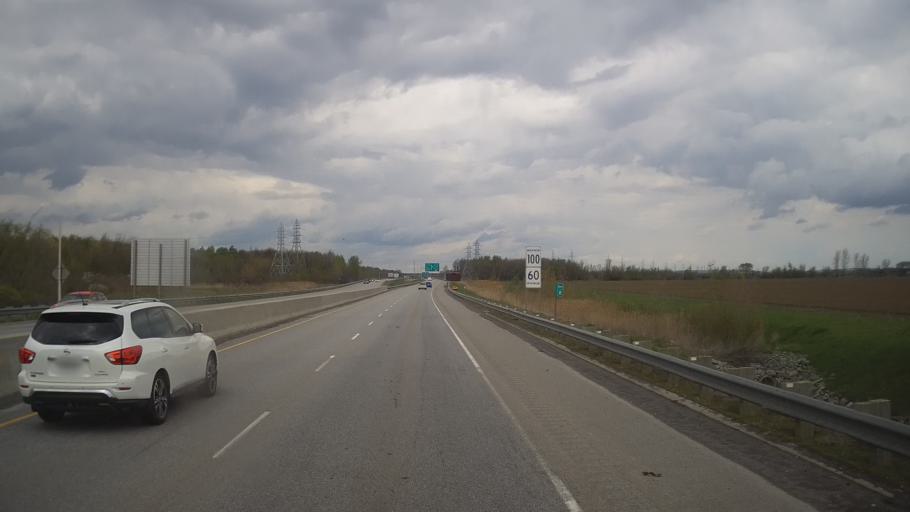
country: CA
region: Quebec
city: Les Cedres
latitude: 45.3350
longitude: -74.0356
